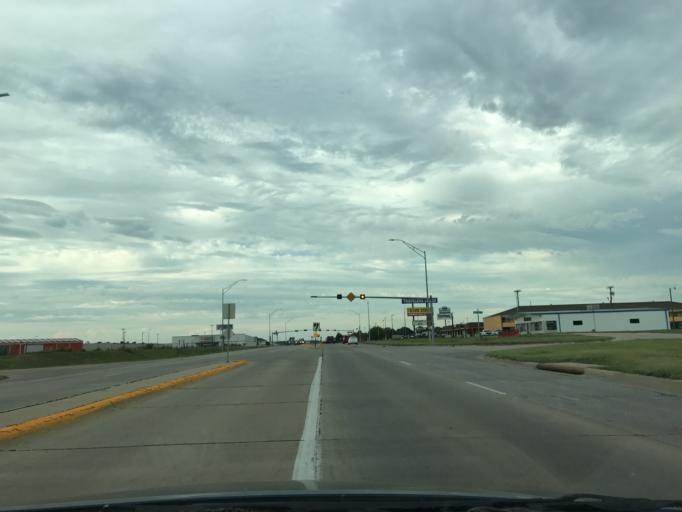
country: US
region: Nebraska
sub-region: Gage County
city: Beatrice
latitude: 40.2997
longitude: -96.7467
